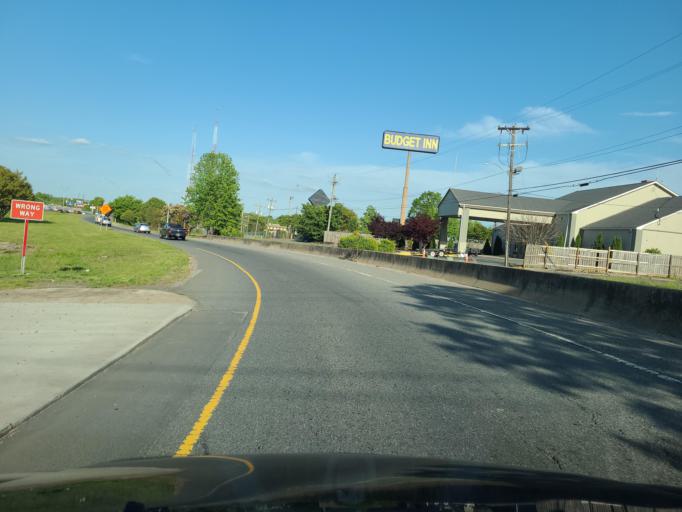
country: US
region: North Carolina
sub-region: Mecklenburg County
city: Charlotte
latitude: 35.2755
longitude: -80.8084
